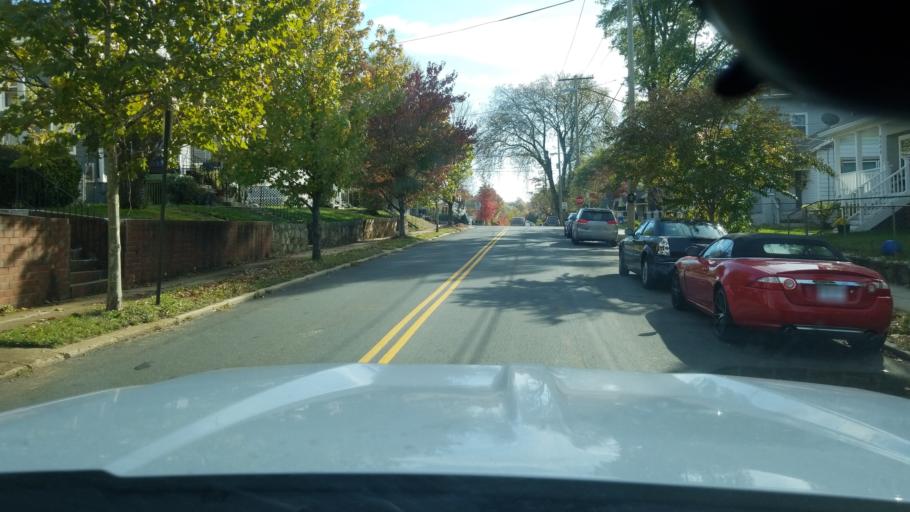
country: US
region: Maryland
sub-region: Prince George's County
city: Mount Rainier
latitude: 38.9390
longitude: -76.9742
